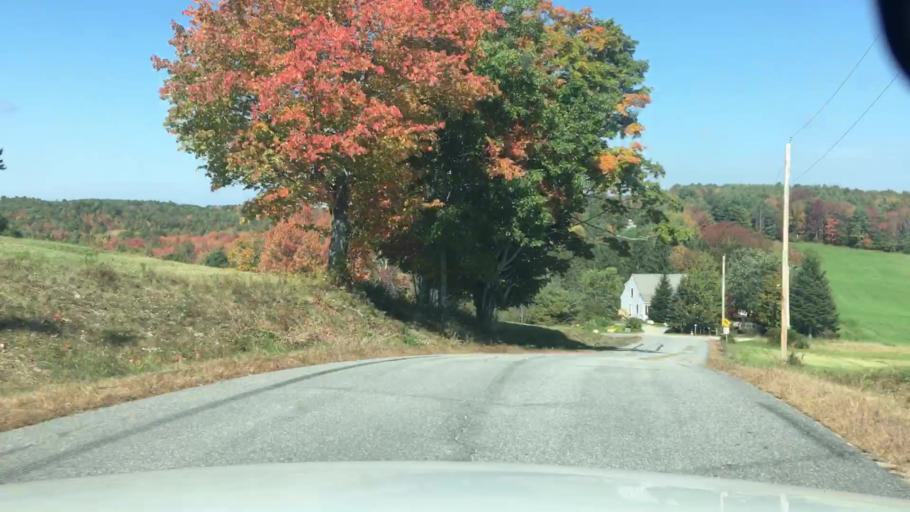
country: US
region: Maine
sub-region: Sagadahoc County
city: Topsham
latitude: 44.0112
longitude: -69.9616
